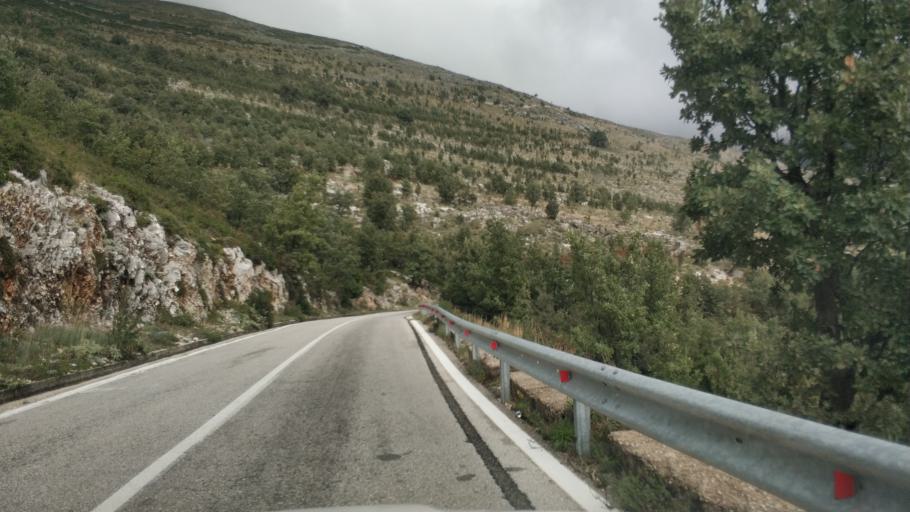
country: AL
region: Vlore
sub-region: Rrethi i Vlores
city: Vranisht
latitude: 40.1840
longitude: 19.6062
